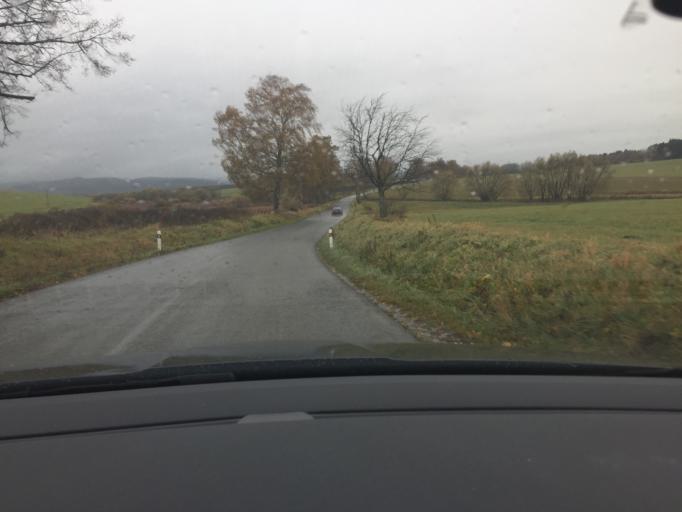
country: SK
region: Presovsky
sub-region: Okres Presov
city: Kezmarok
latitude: 49.1856
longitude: 20.3939
